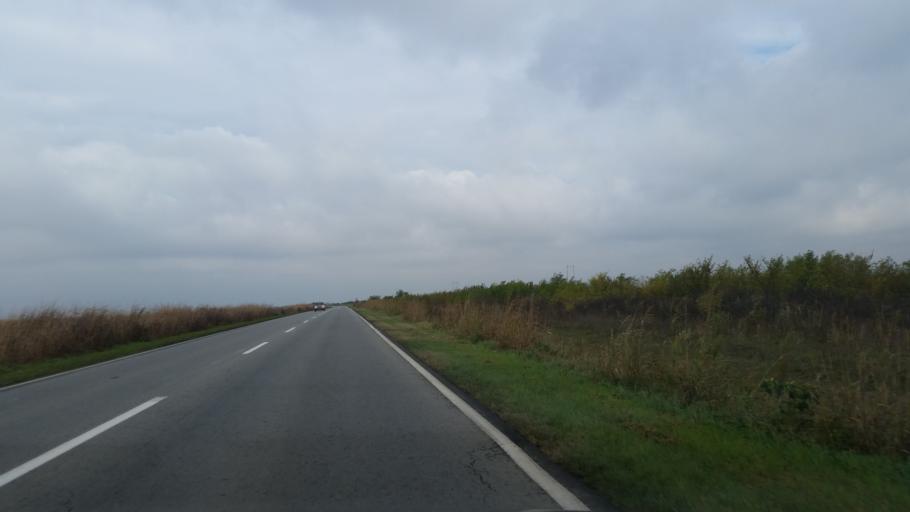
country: RS
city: Elemir
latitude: 45.4485
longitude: 20.3579
